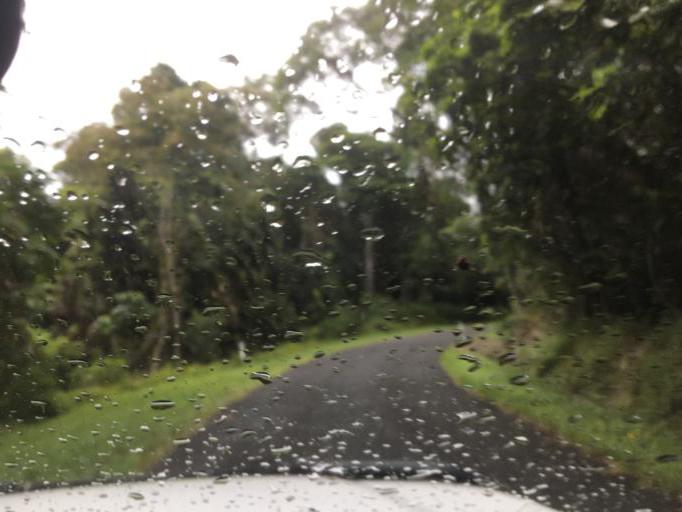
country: AU
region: Queensland
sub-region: Tablelands
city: Kuranda
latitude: -16.8367
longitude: 145.6421
